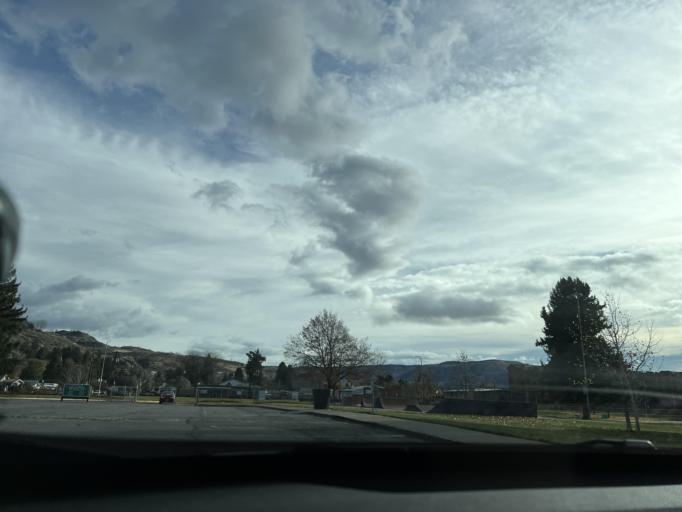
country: US
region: Washington
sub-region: Chelan County
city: Chelan
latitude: 47.8445
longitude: -120.0258
